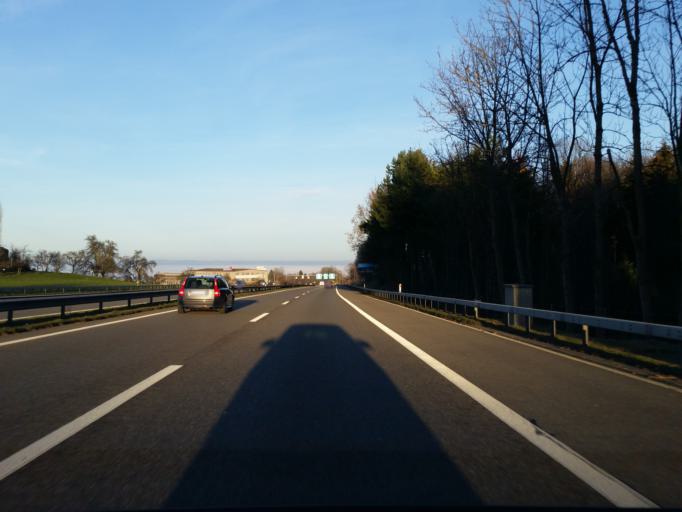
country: CH
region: Saint Gallen
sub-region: Wahlkreis Rorschach
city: Morschwil
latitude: 47.4536
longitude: 9.4273
